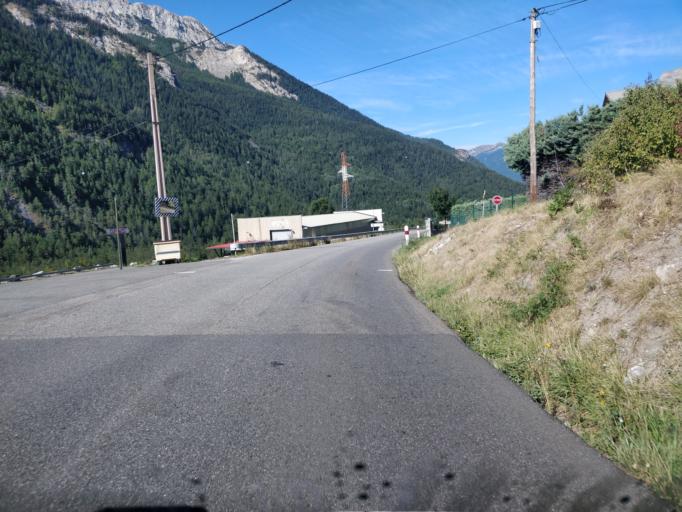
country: FR
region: Provence-Alpes-Cote d'Azur
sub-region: Departement des Alpes-de-Haute-Provence
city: Barcelonnette
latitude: 44.3925
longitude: 6.5655
